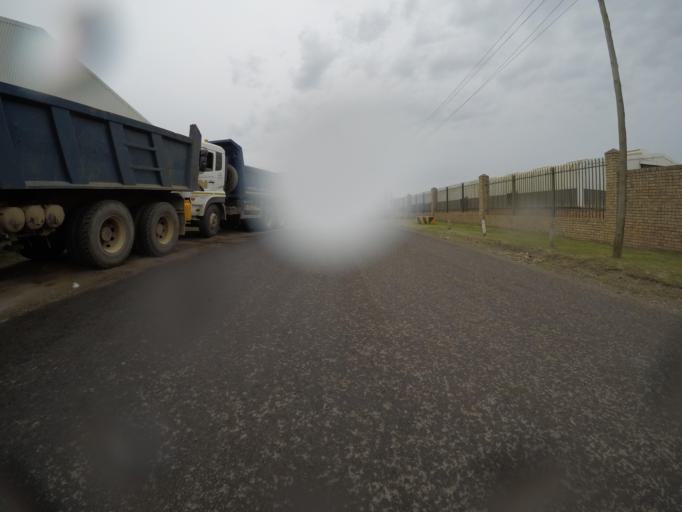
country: ZA
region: Eastern Cape
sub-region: Buffalo City Metropolitan Municipality
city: East London
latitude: -32.9781
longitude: 27.8236
